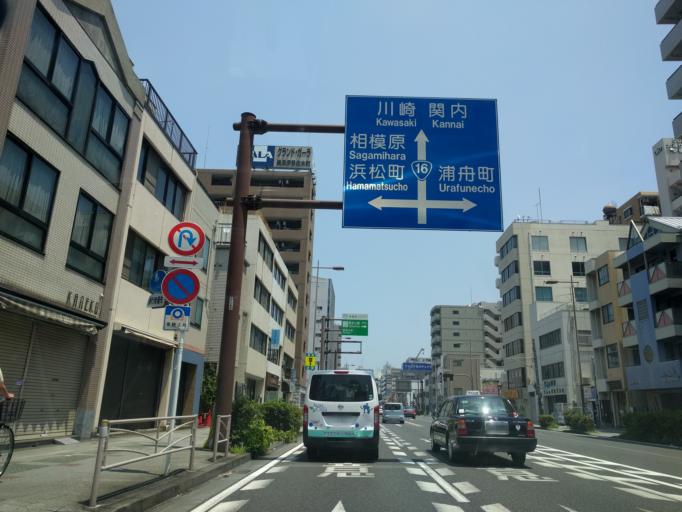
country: JP
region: Kanagawa
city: Yokohama
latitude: 35.4379
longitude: 139.6237
